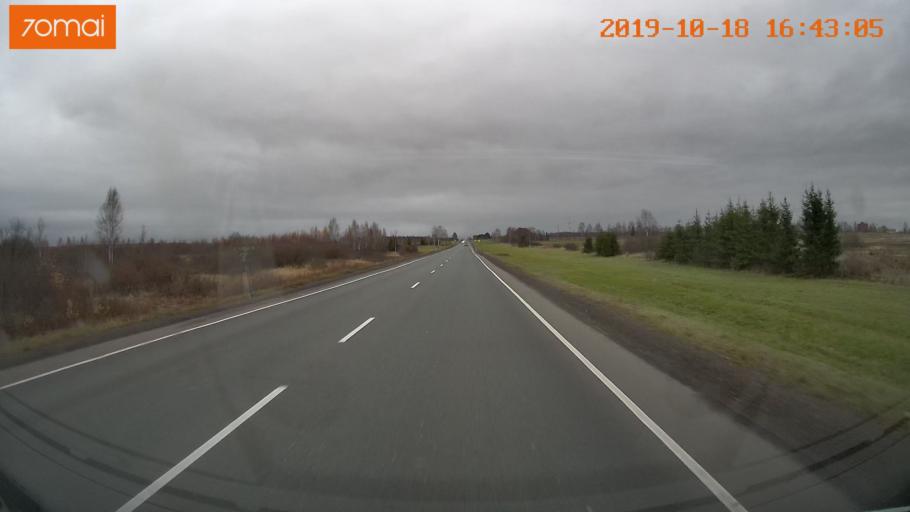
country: RU
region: Vladimir
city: Kideksha
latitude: 56.4867
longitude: 40.5088
